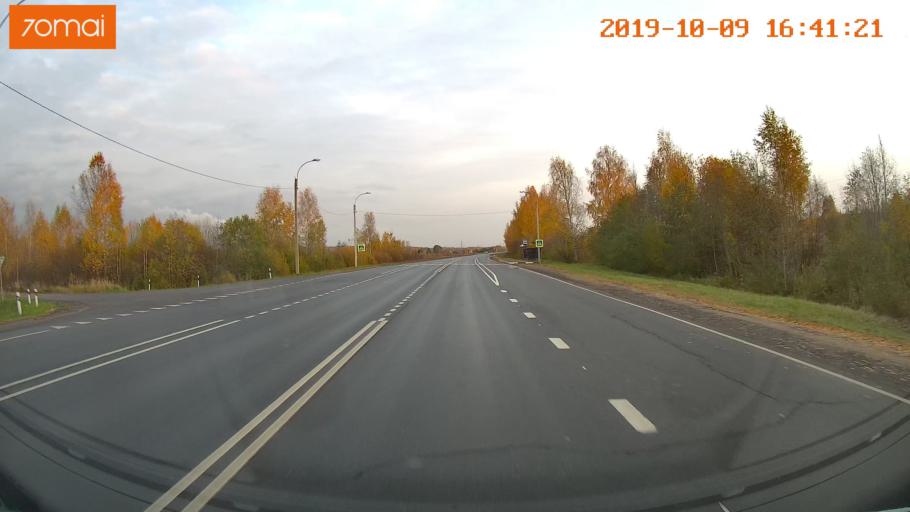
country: RU
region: Kostroma
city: Volgorechensk
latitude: 57.4738
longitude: 41.0794
